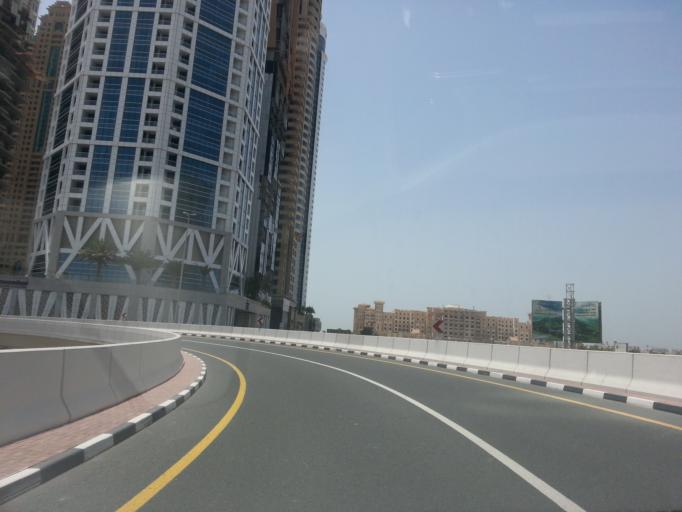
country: AE
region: Dubai
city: Dubai
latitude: 25.0893
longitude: 55.1520
